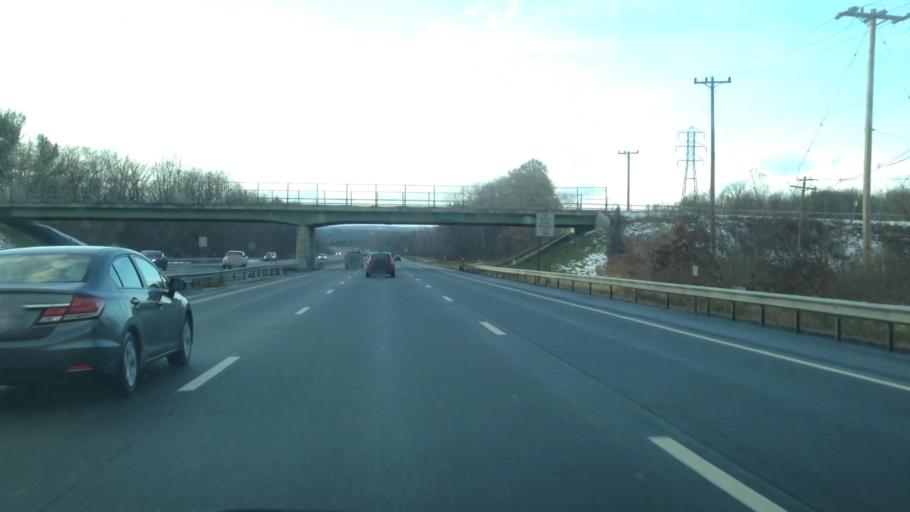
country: US
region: New York
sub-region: Schenectady County
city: Rotterdam
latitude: 42.7712
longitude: -73.9740
